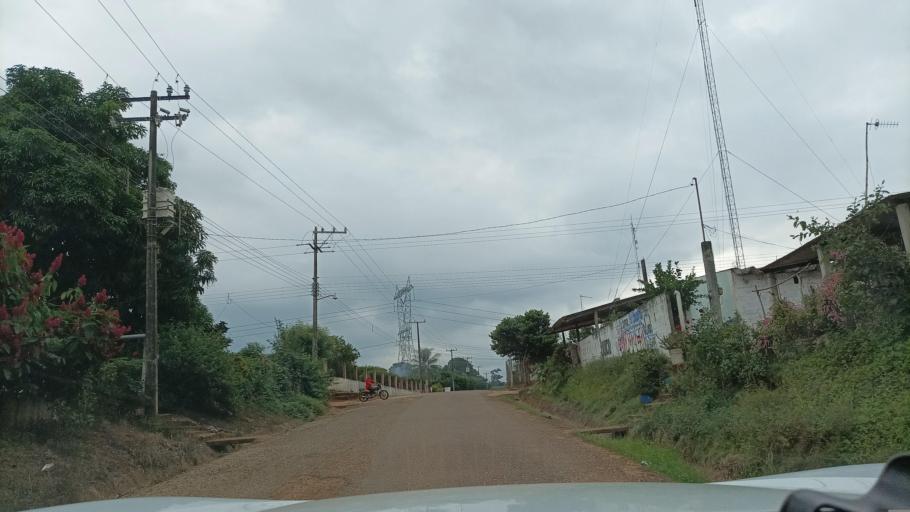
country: MX
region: Veracruz
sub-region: Acayucan
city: Ixhuapan
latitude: 18.0409
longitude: -94.8201
